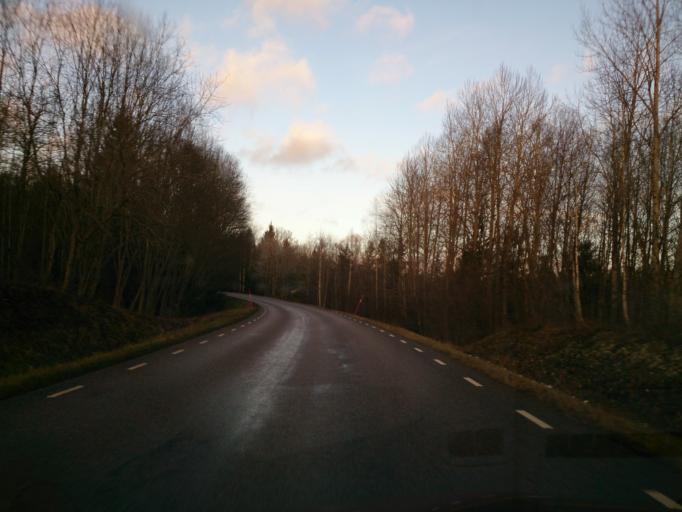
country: SE
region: OEstergoetland
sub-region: Atvidabergs Kommun
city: Atvidaberg
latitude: 58.2334
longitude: 16.0083
